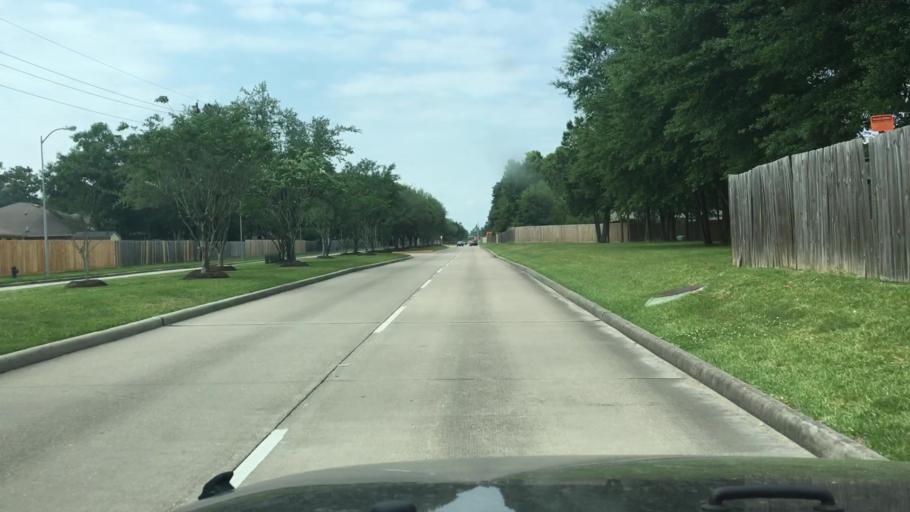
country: US
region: Texas
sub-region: Harris County
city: Atascocita
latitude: 29.9656
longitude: -95.2104
